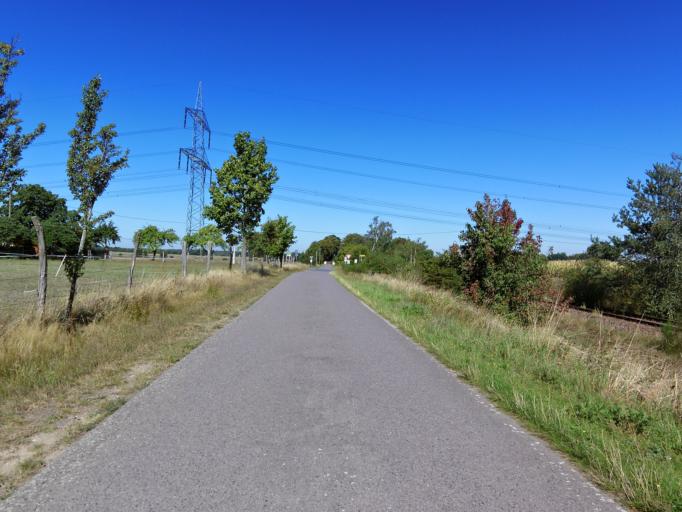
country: DE
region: Saxony
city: Dommitzsch
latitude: 51.6601
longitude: 12.8427
